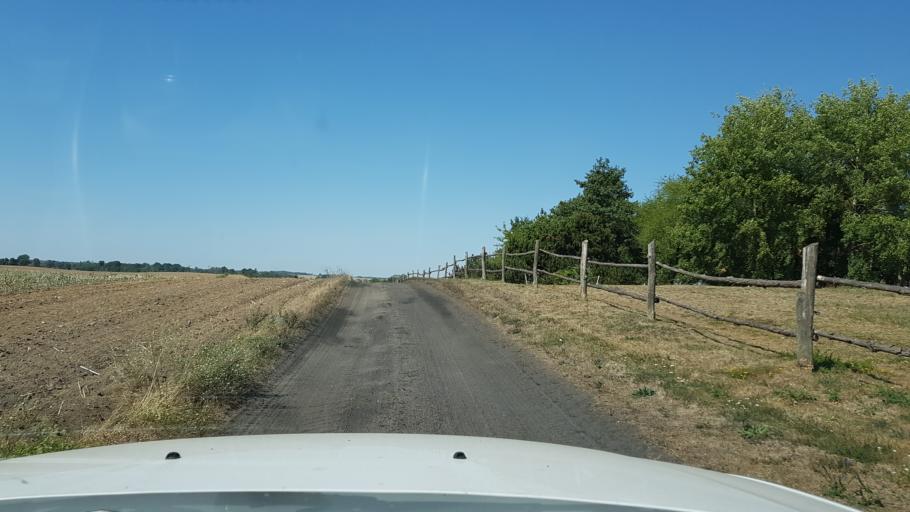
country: PL
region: West Pomeranian Voivodeship
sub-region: Powiat gryfinski
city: Moryn
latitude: 52.8547
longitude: 14.3564
